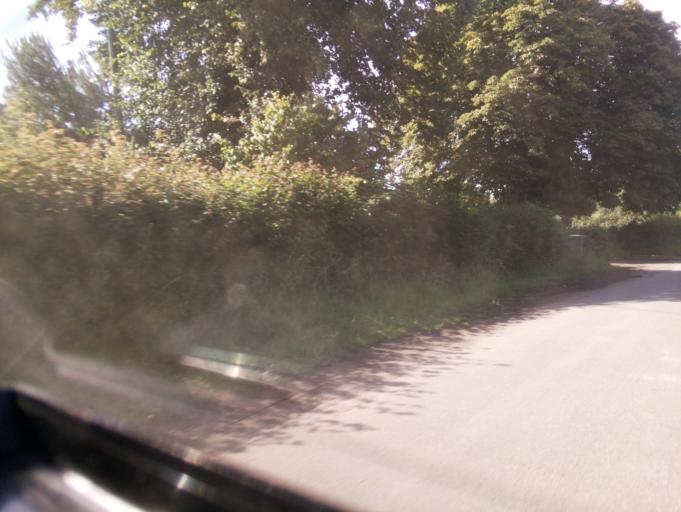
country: GB
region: England
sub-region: South Gloucestershire
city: Bitton
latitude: 51.4351
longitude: -2.4501
